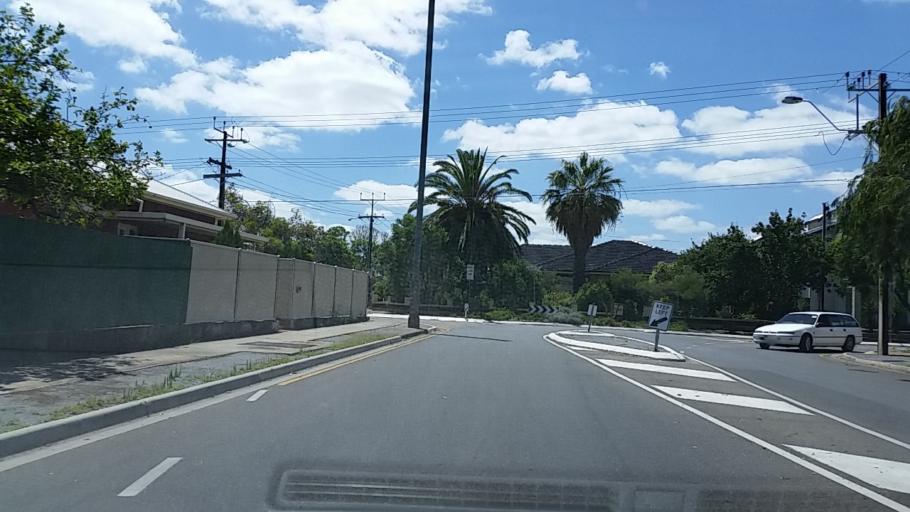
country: AU
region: South Australia
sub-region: City of West Torrens
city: Thebarton
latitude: -34.9292
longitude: 138.5606
